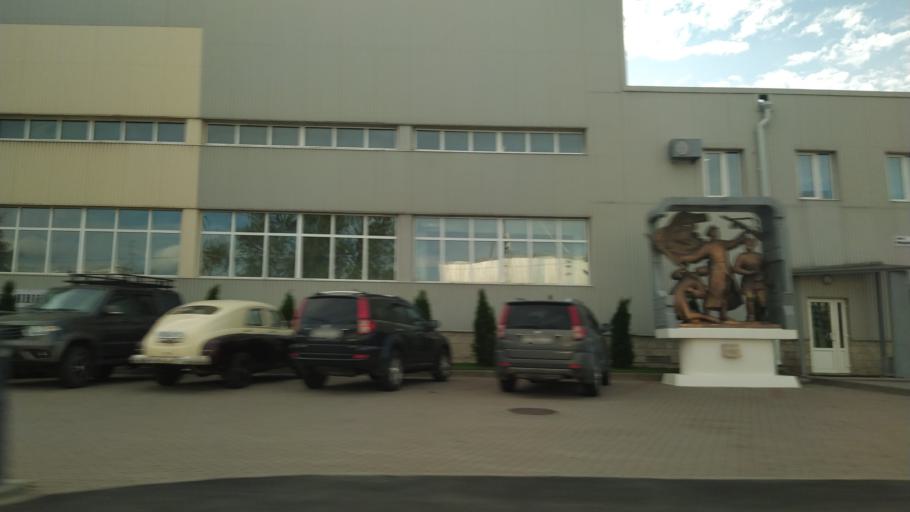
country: RU
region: Leningrad
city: Finlyandskiy
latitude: 59.9623
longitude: 30.3972
